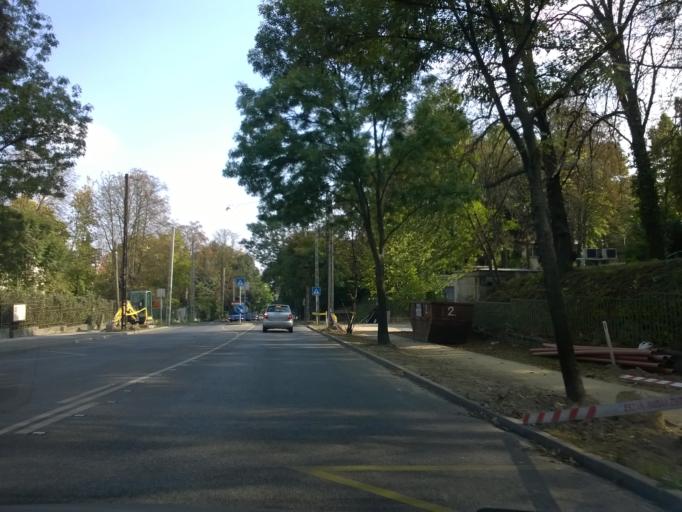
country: HU
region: Budapest
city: Budapest XII. keruelet
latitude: 47.5259
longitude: 18.9843
